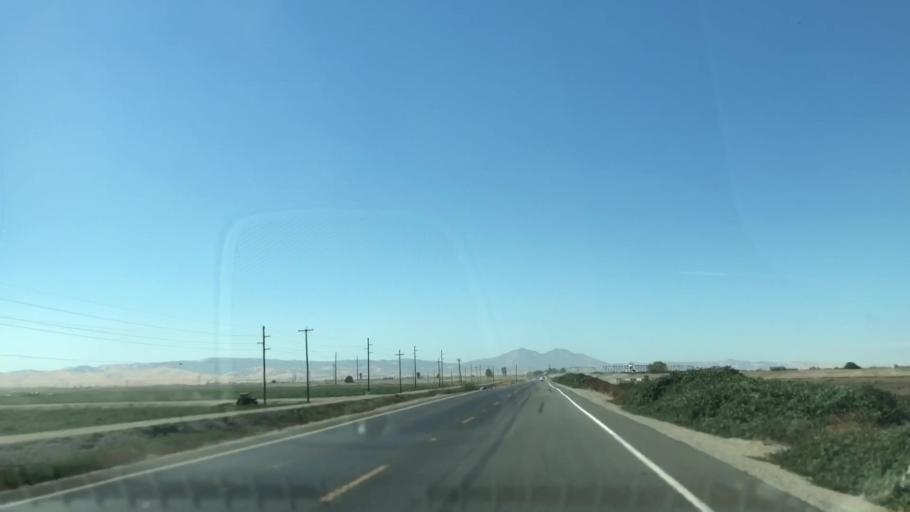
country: US
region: California
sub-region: Contra Costa County
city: Discovery Bay
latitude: 37.8901
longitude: -121.5585
